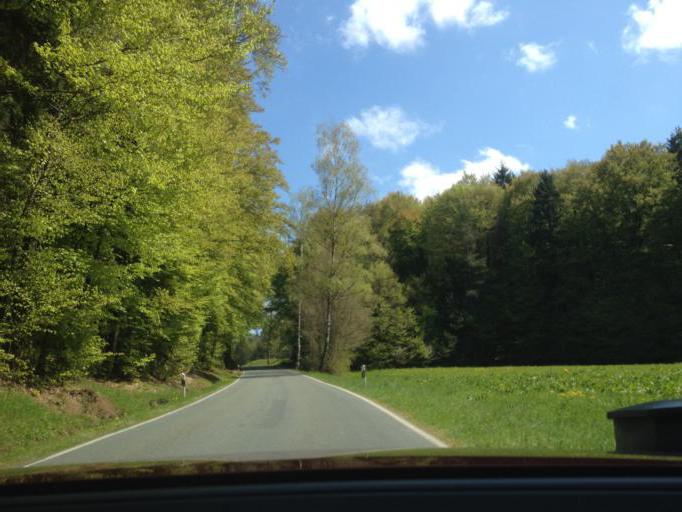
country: DE
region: Bavaria
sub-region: Upper Franconia
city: Obertrubach
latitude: 49.6757
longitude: 11.4102
